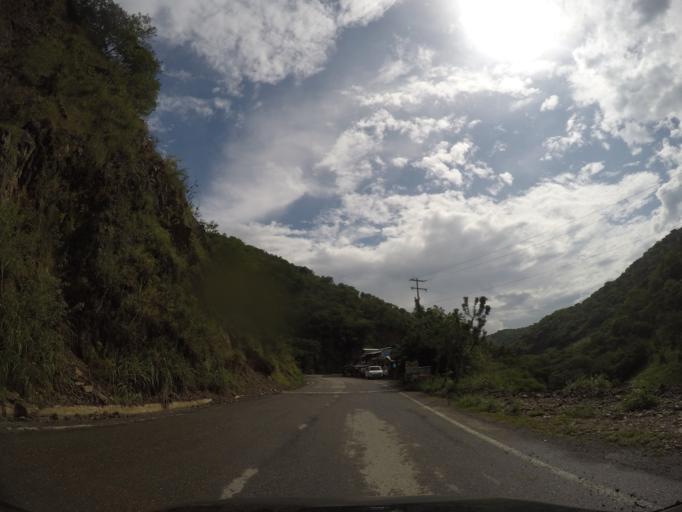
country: MX
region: Oaxaca
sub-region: San Jeronimo Coatlan
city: San Cristobal Honduras
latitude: 16.3735
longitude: -97.0793
